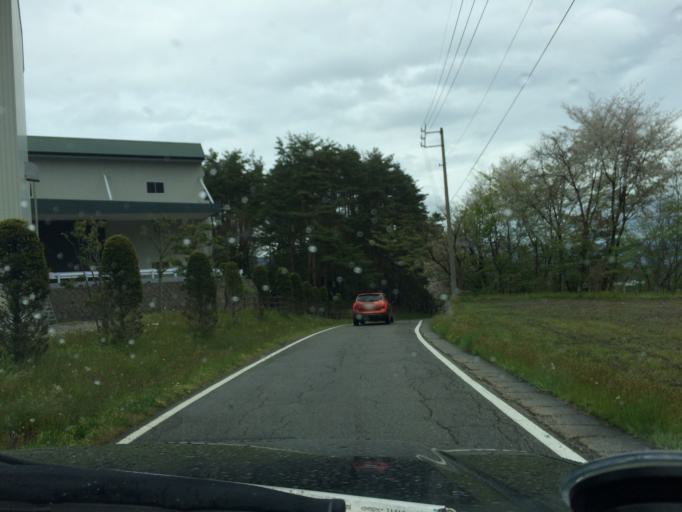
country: JP
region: Nagano
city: Omachi
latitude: 36.5151
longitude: 137.8110
